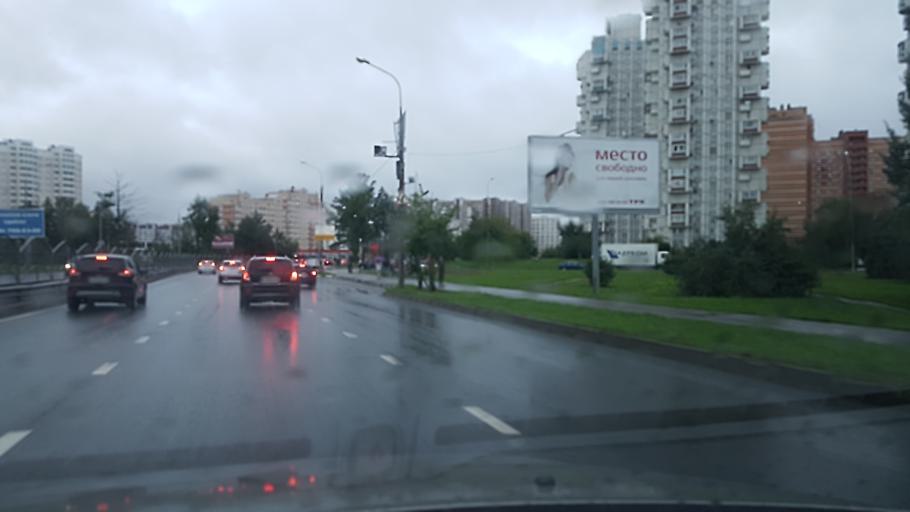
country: RU
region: Moscow
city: Zelenograd
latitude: 55.9782
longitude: 37.1684
